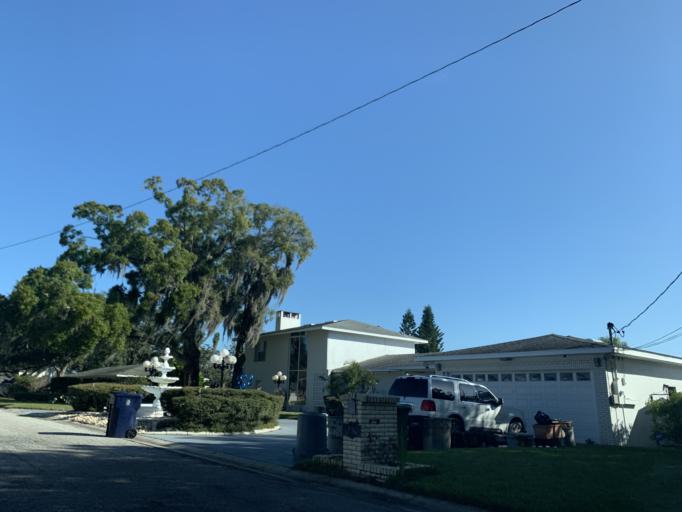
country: US
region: Florida
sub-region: Hillsborough County
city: Temple Terrace
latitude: 28.0193
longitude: -82.4122
